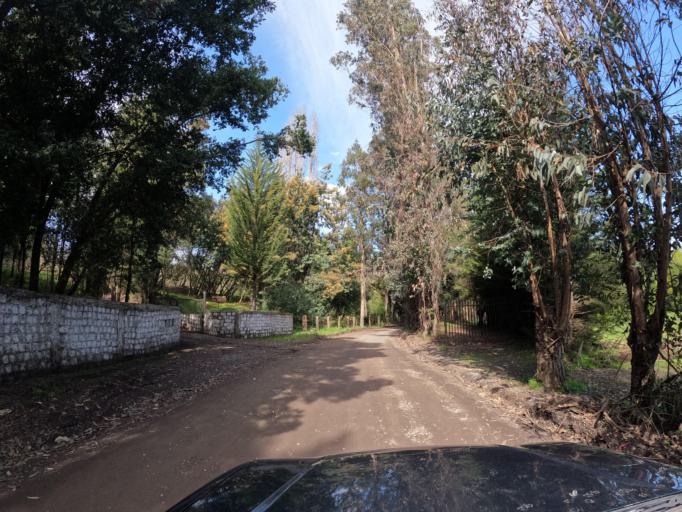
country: CL
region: Biobio
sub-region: Provincia de Concepcion
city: Chiguayante
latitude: -37.0511
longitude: -72.9545
